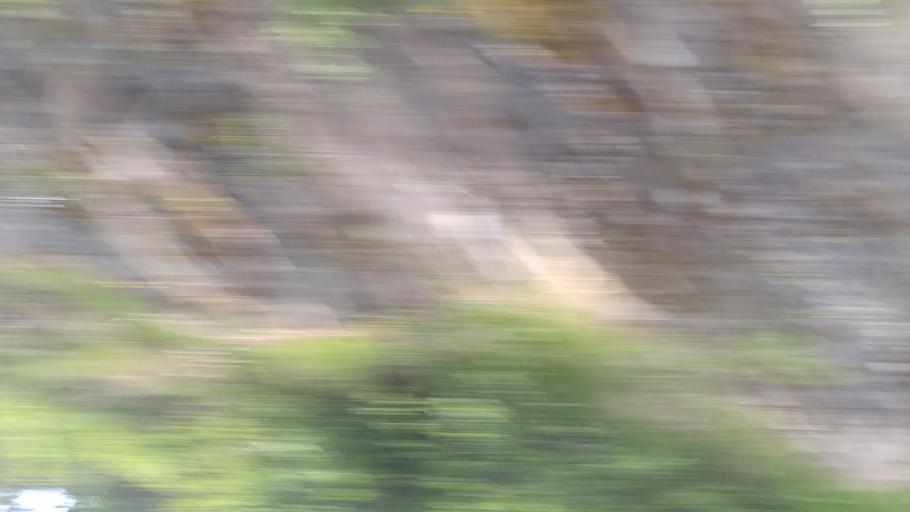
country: NO
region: Nord-Trondelag
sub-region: Levanger
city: Skogn
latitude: 63.4567
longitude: 11.3292
